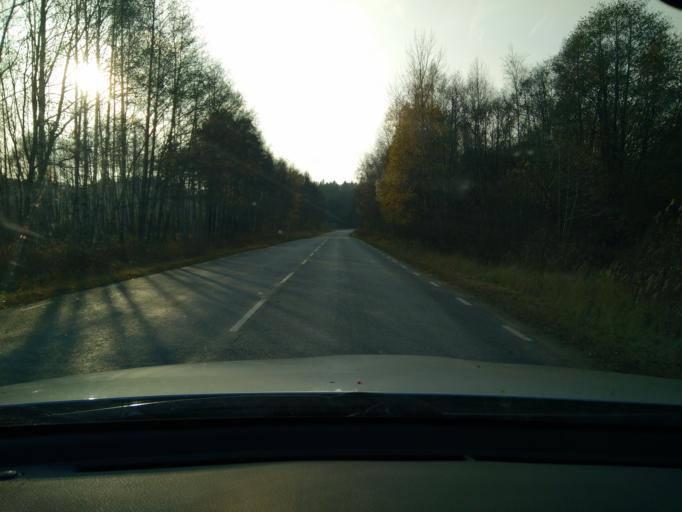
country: SE
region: Stockholm
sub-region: Sollentuna Kommun
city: Sollentuna
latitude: 59.4571
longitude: 17.9678
